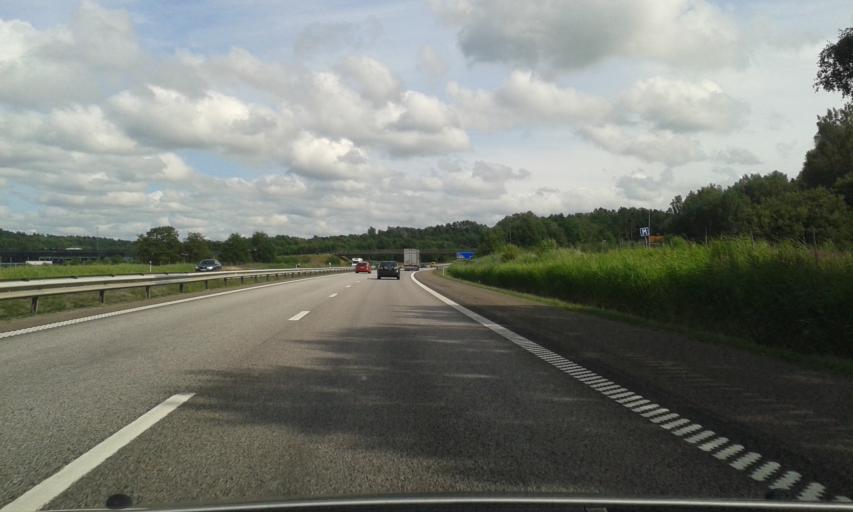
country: SE
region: Halland
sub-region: Kungsbacka Kommun
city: Fjaeras kyrkby
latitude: 57.4345
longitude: 12.1465
